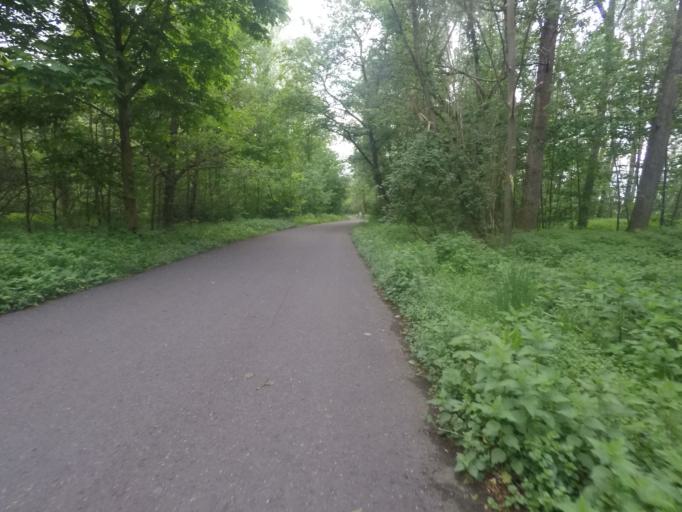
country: DE
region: North Rhine-Westphalia
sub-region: Regierungsbezirk Koln
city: Porz am Rhein
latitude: 50.8883
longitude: 7.0452
